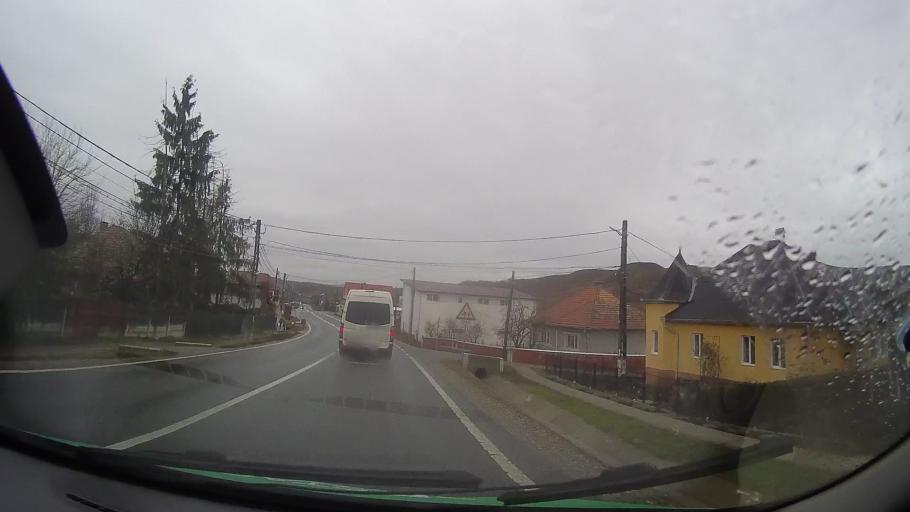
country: RO
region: Bistrita-Nasaud
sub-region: Comuna Galatii Bistritei
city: Galatii Bistritei
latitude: 47.0194
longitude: 24.4140
